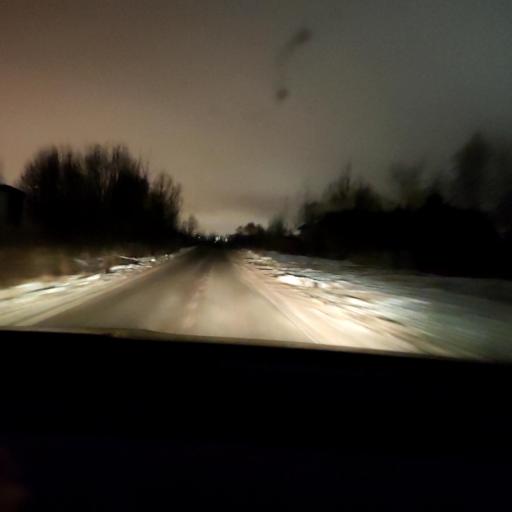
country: RU
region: Moskovskaya
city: Novopodrezkovo
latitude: 55.9136
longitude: 37.3664
